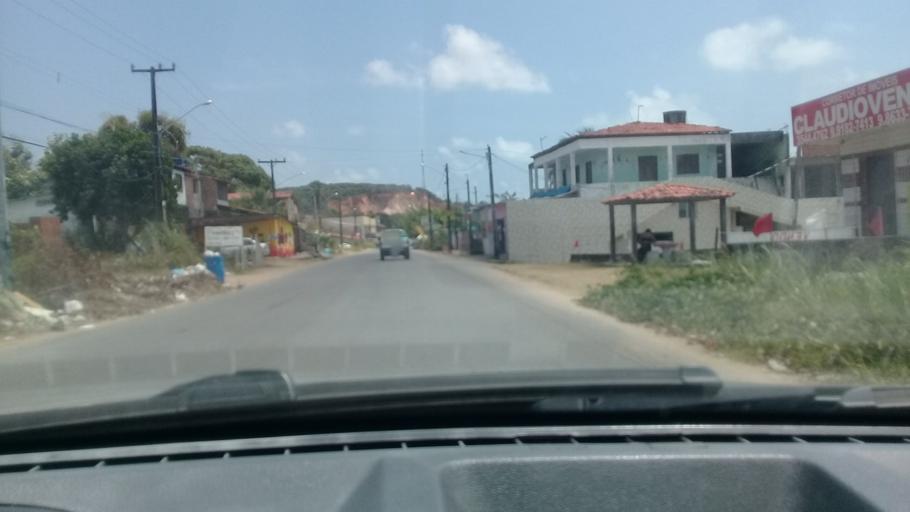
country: BR
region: Pernambuco
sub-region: Itamaraca
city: Itamaraca
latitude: -7.7891
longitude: -34.8407
